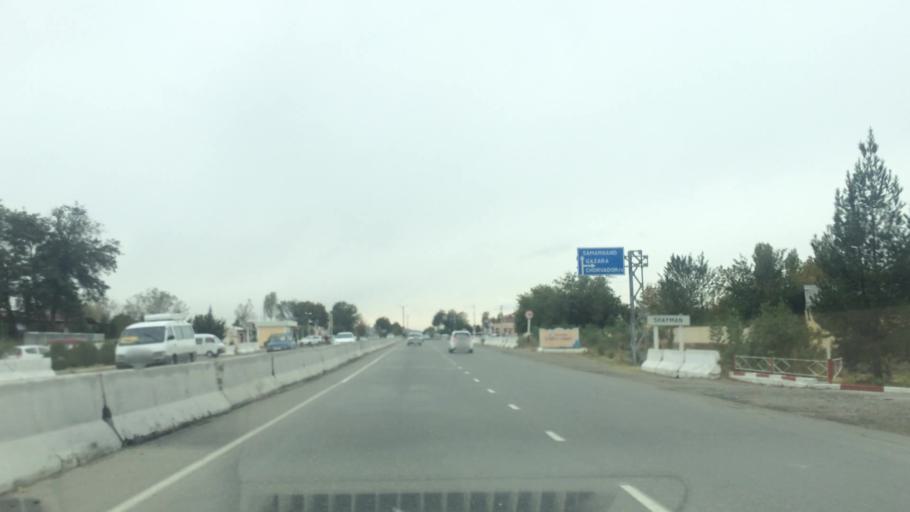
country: UZ
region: Samarqand
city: Jomboy
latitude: 39.7153
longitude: 67.1047
